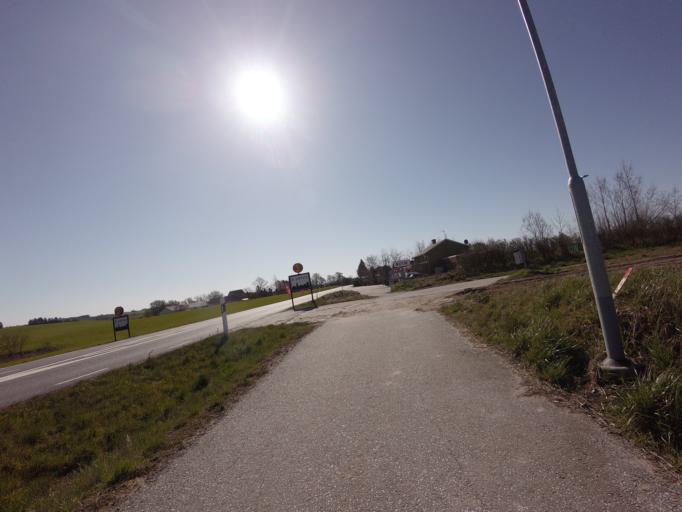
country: SE
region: Skane
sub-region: Malmo
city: Oxie
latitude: 55.4733
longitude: 13.1335
